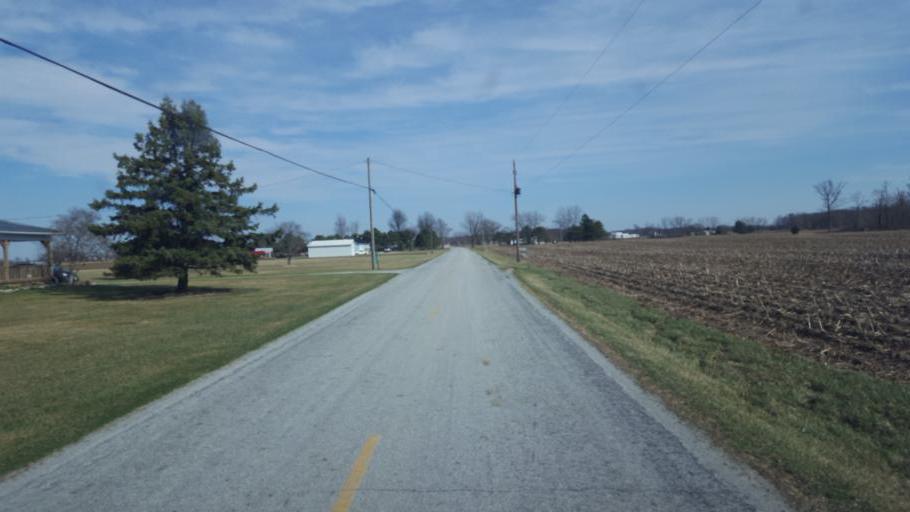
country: US
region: Ohio
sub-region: Hardin County
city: Kenton
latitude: 40.6576
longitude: -83.4711
